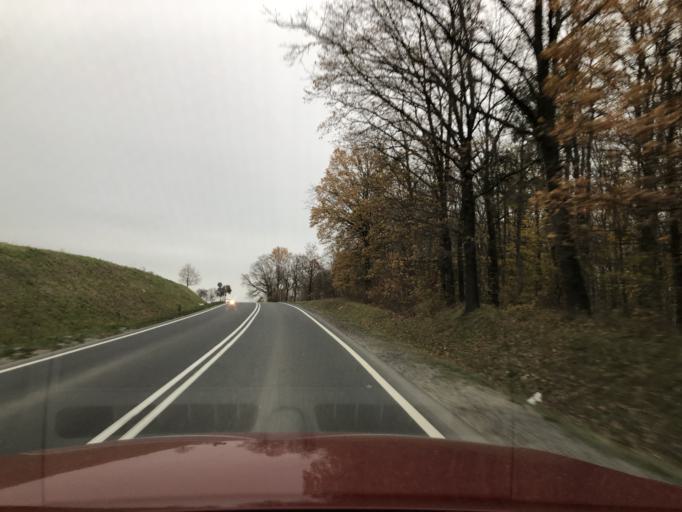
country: PL
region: Lower Silesian Voivodeship
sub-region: Powiat swidnicki
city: Zarow
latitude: 50.9729
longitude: 16.4981
